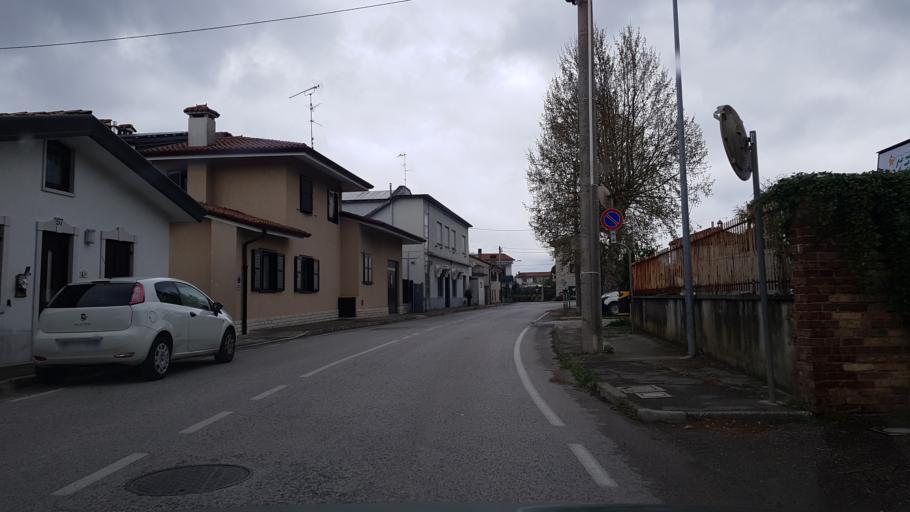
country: IT
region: Friuli Venezia Giulia
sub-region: Provincia di Gorizia
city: Turriaco
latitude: 45.8224
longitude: 13.4435
